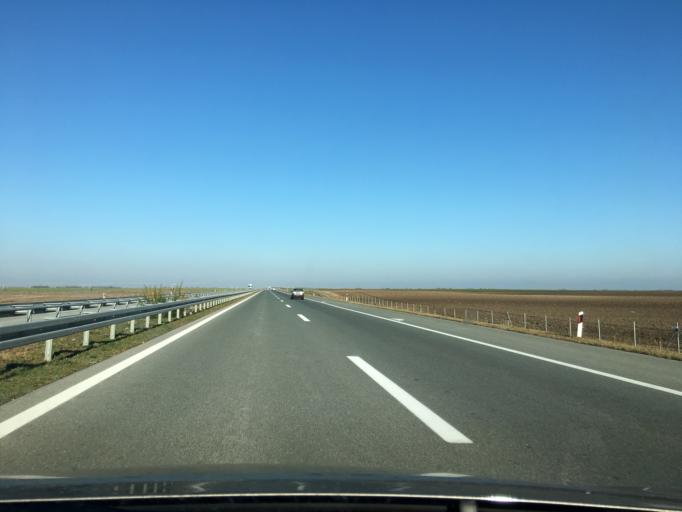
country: RS
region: Autonomna Pokrajina Vojvodina
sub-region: Severnobacki Okrug
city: Mali Igos
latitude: 45.7064
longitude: 19.7173
